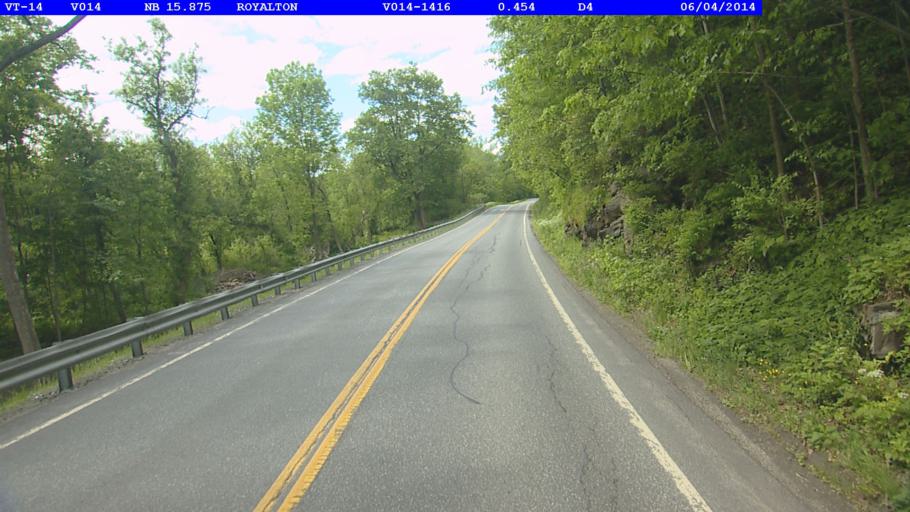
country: US
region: Vermont
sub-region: Windsor County
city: Woodstock
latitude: 43.8010
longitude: -72.5011
